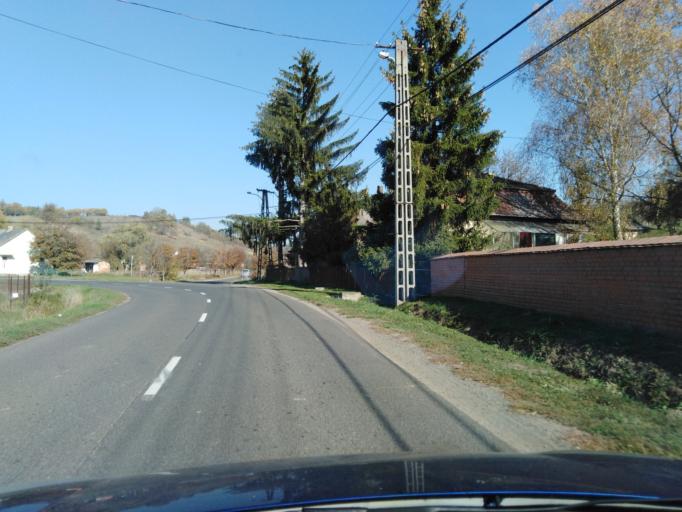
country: HU
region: Nograd
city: Karancskeszi
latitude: 48.1598
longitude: 19.7091
